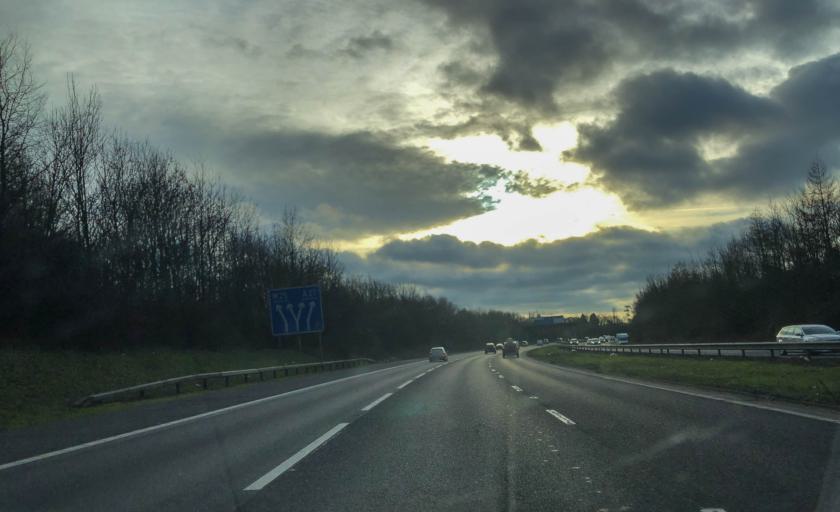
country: GB
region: England
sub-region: Kent
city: Shoreham
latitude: 51.3072
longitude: 0.1591
